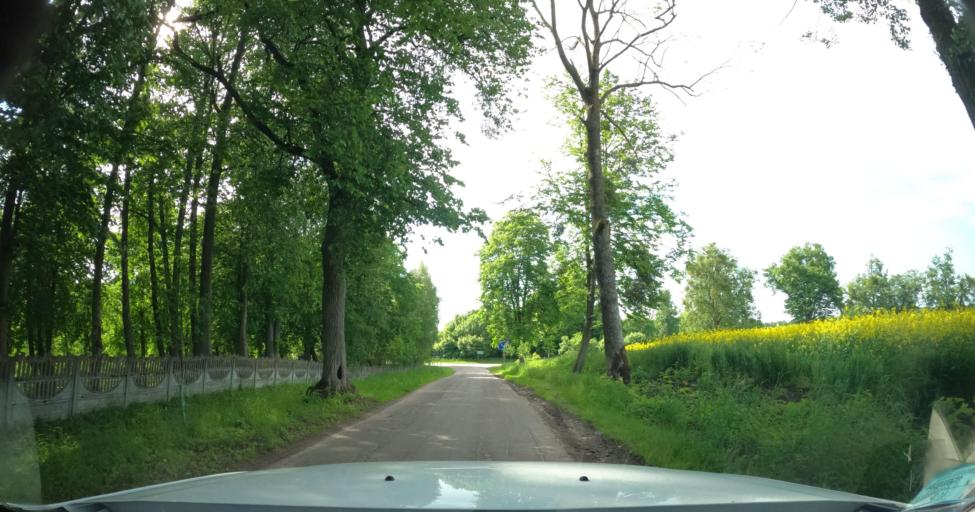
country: PL
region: Warmian-Masurian Voivodeship
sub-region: Powiat ostrodzki
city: Morag
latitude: 54.0198
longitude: 19.9153
